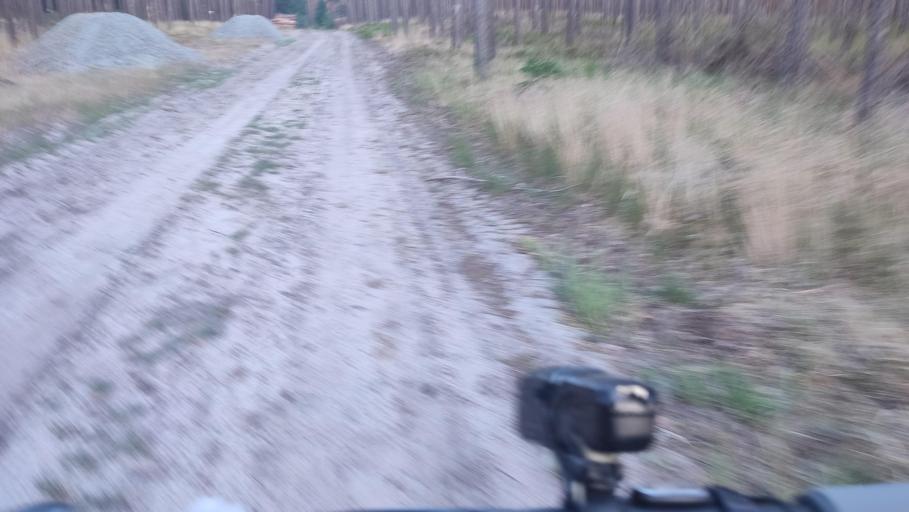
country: DE
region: Lower Saxony
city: Hitzacker
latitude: 53.2210
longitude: 11.0386
